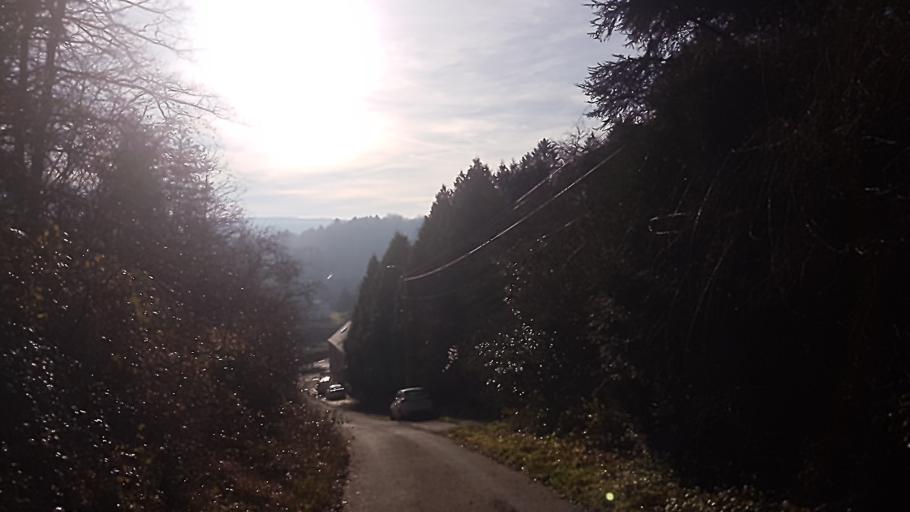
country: BE
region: Wallonia
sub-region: Province de Namur
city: Couvin
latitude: 50.0774
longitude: 4.6070
